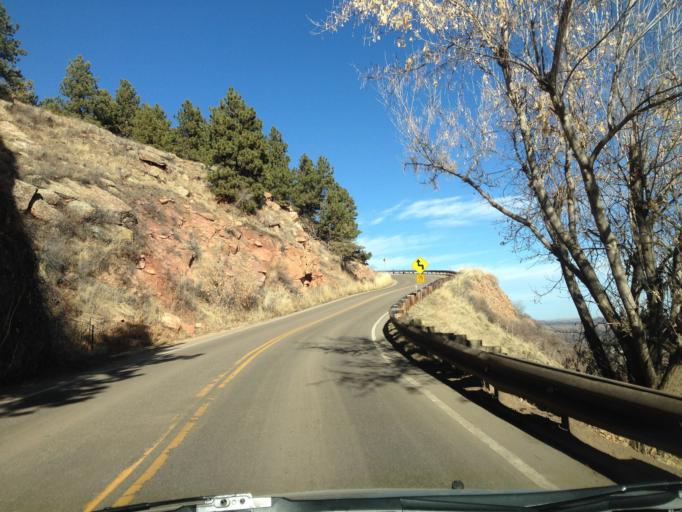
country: US
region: Colorado
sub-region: Boulder County
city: Boulder
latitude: 40.0032
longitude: -105.2924
